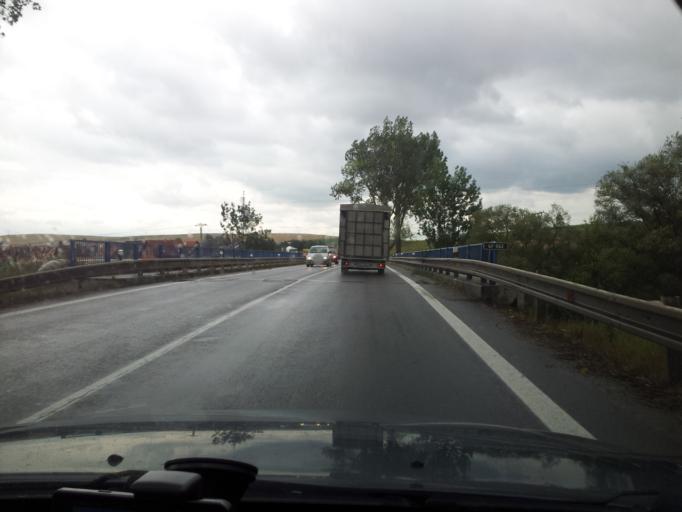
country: SK
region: Presovsky
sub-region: Okres Presov
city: Kezmarok
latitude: 49.1117
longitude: 20.3656
